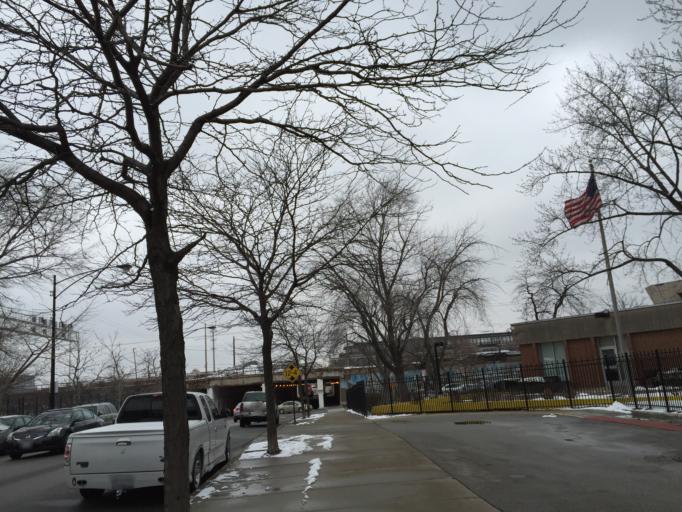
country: US
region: Illinois
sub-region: Cook County
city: Chicago
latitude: 41.8591
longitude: -87.6564
